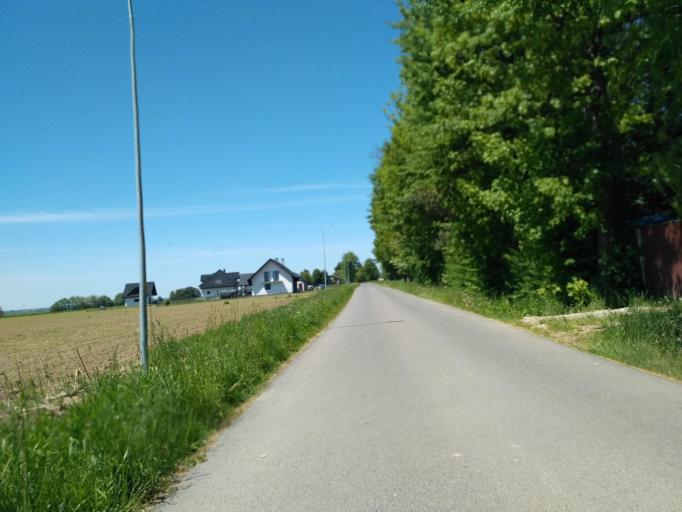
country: PL
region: Subcarpathian Voivodeship
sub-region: Powiat sanocki
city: Dlugie
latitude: 49.5942
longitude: 22.0481
